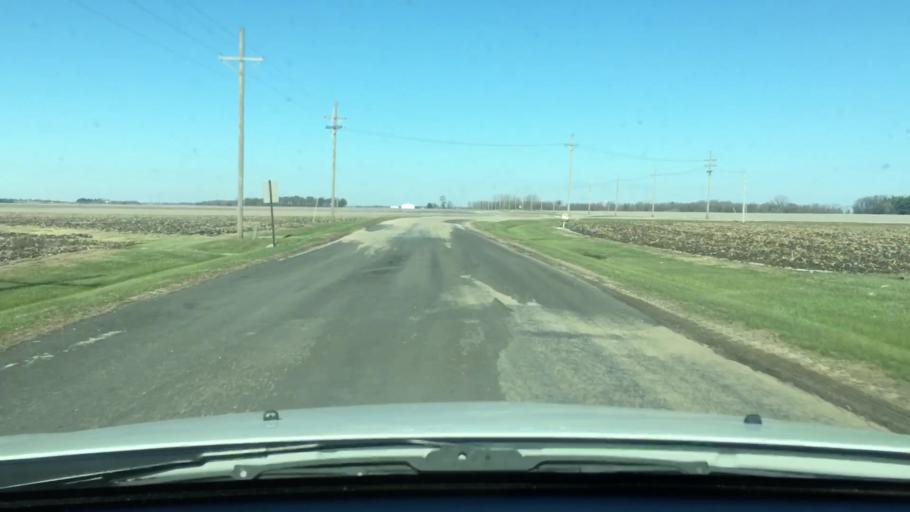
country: US
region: Illinois
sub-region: Ogle County
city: Hillcrest
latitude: 41.9770
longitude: -89.0009
